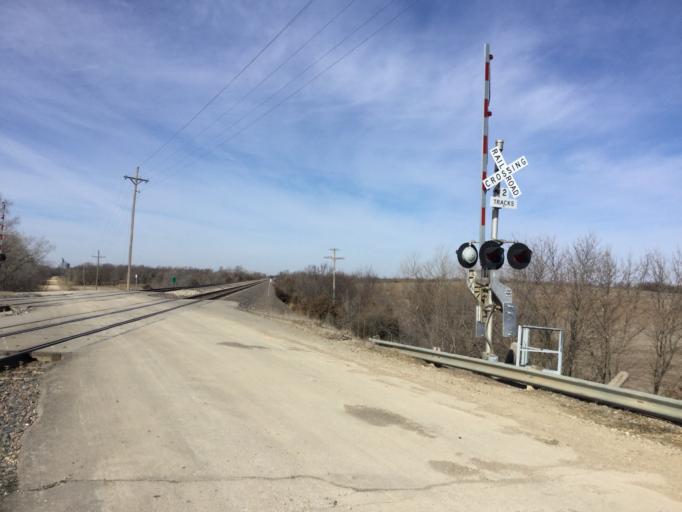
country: US
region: Kansas
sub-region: Marshall County
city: Marysville
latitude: 39.9002
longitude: -96.7725
